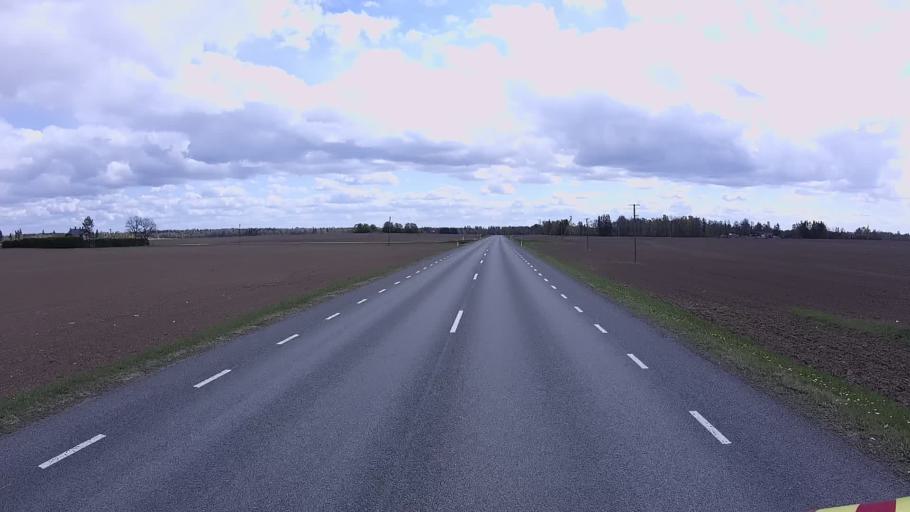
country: EE
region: Jaervamaa
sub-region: Jaerva-Jaani vald
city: Jarva-Jaani
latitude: 59.0886
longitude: 25.8342
